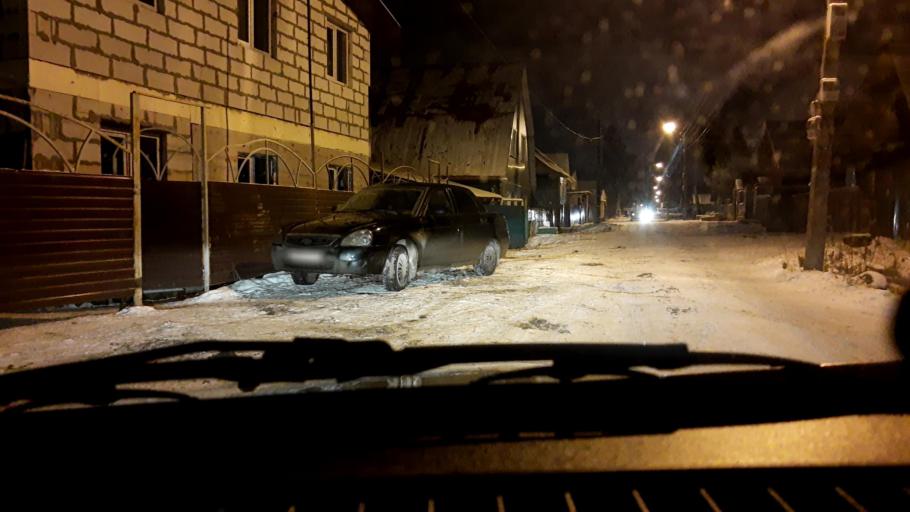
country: RU
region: Bashkortostan
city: Iglino
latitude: 54.8283
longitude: 56.1895
